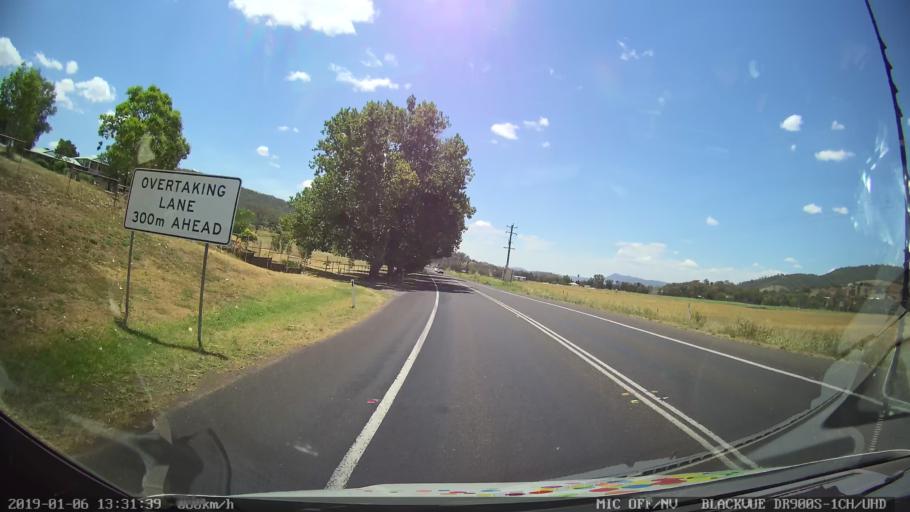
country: AU
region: New South Wales
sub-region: Tamworth Municipality
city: East Tamworth
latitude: -31.1193
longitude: 150.9952
